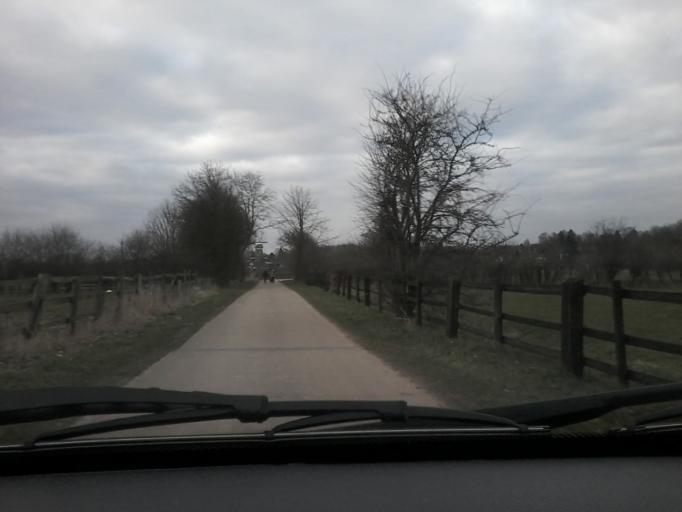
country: DE
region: Lower Saxony
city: Achim
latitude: 52.9977
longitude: 9.0375
